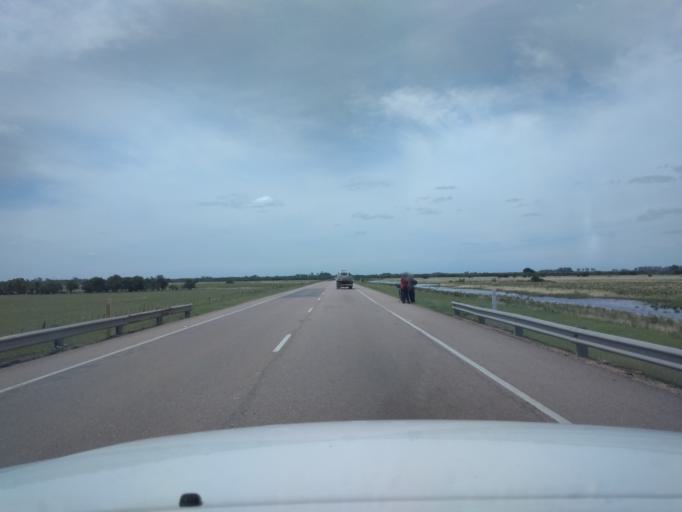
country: UY
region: Canelones
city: Canelones
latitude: -34.3808
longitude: -56.2525
